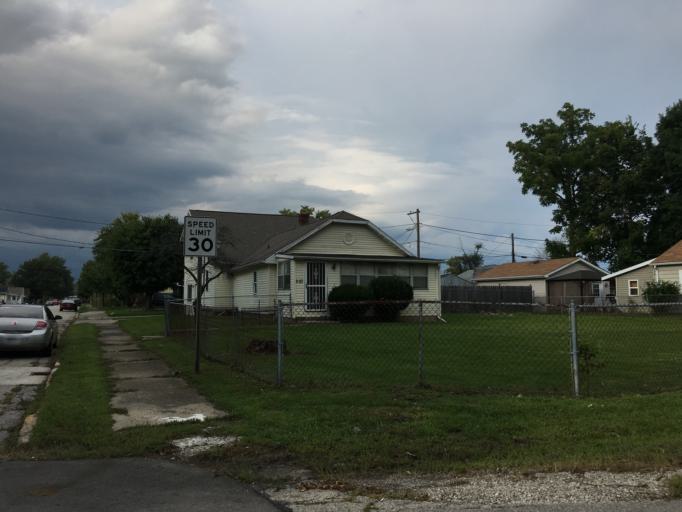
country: US
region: Indiana
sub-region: Howard County
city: Kokomo
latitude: 40.4625
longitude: -86.1257
